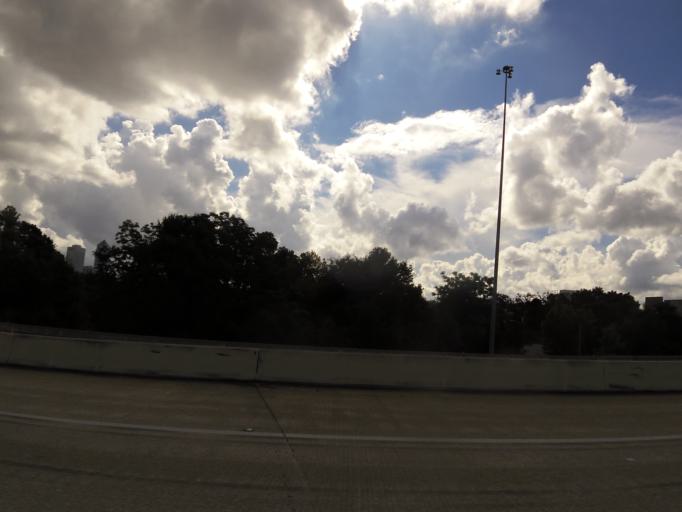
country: US
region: Florida
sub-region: Duval County
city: Jacksonville
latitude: 30.3256
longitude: -81.6794
